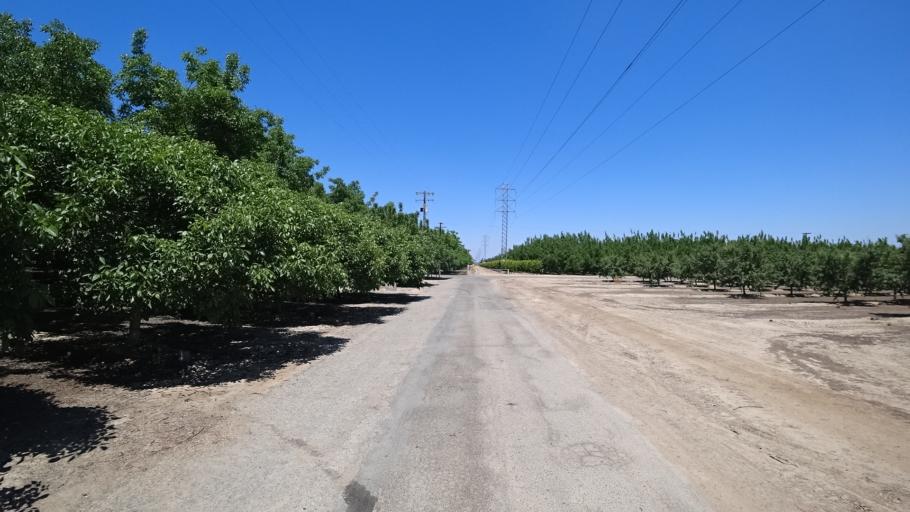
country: US
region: California
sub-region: Fresno County
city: Kingsburg
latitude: 36.4446
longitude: -119.5916
